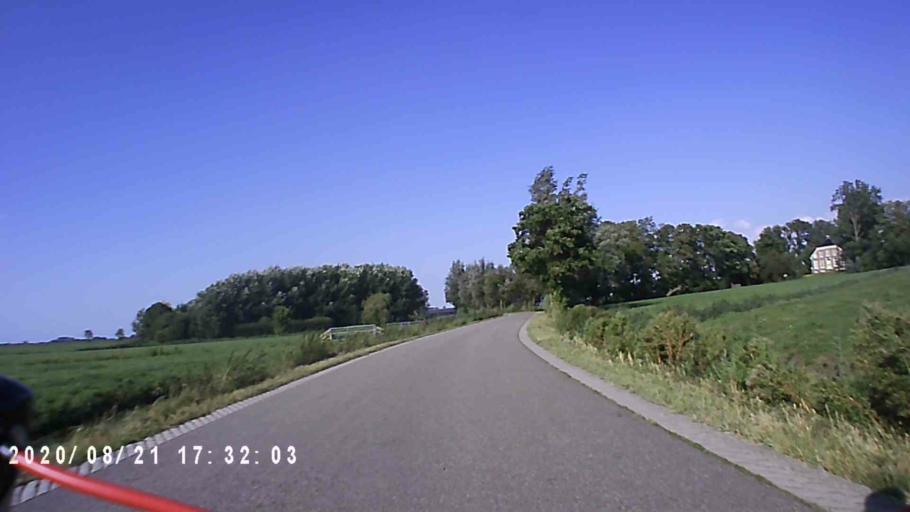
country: NL
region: Groningen
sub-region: Gemeente Bedum
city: Bedum
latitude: 53.2756
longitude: 6.5899
